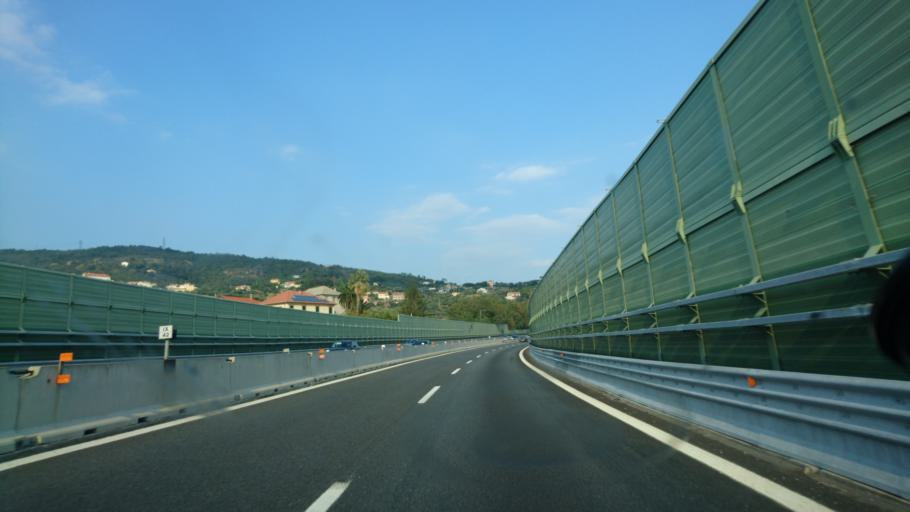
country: IT
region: Liguria
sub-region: Provincia di Savona
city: Savona
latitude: 44.3027
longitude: 8.4492
